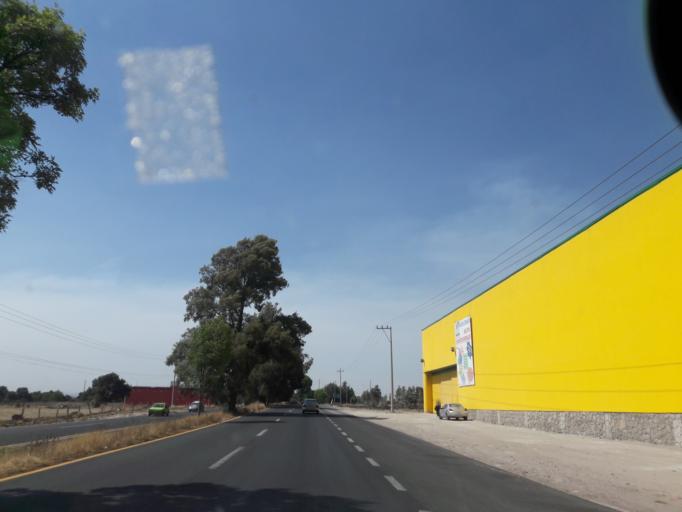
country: MX
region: Tlaxcala
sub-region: Mazatecochco de Jose Maria Morelos
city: Mazatecochco
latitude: 19.1908
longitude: -98.1942
